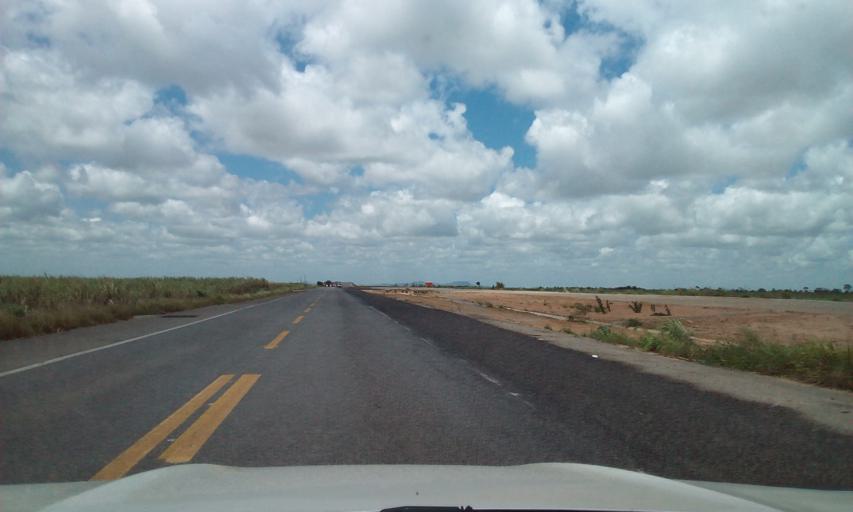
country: BR
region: Alagoas
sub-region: Sao Miguel Dos Campos
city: Sao Miguel dos Campos
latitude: -9.8765
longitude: -36.1377
